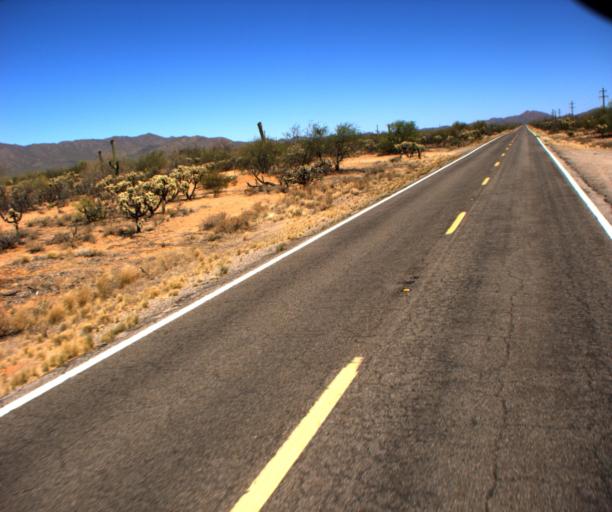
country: US
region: Arizona
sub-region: Pima County
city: Sells
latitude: 32.1084
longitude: -112.0721
